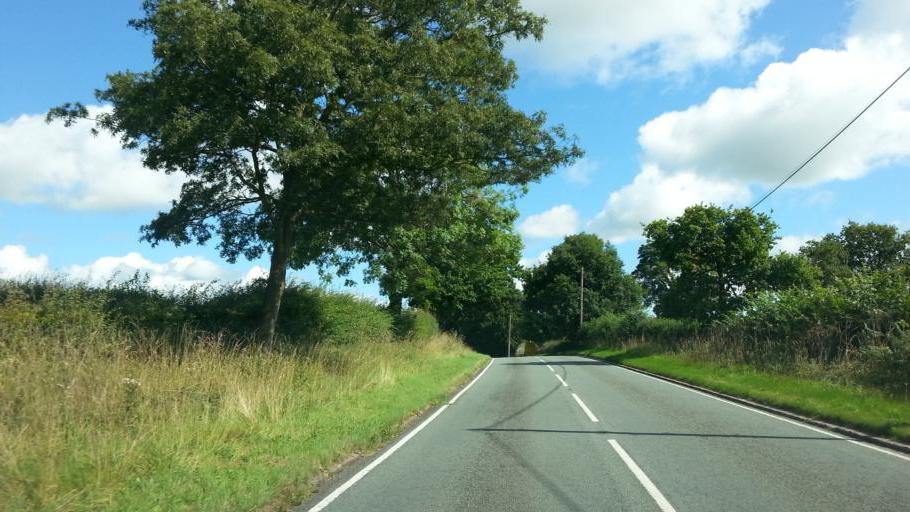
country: GB
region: England
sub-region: Staffordshire
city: Uttoxeter
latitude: 52.8672
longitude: -1.8908
